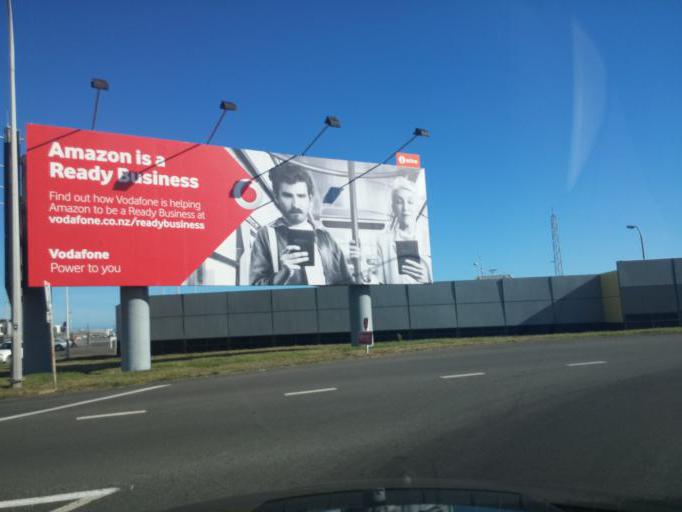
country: NZ
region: Wellington
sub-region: Wellington City
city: Wellington
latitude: -41.3258
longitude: 174.8098
